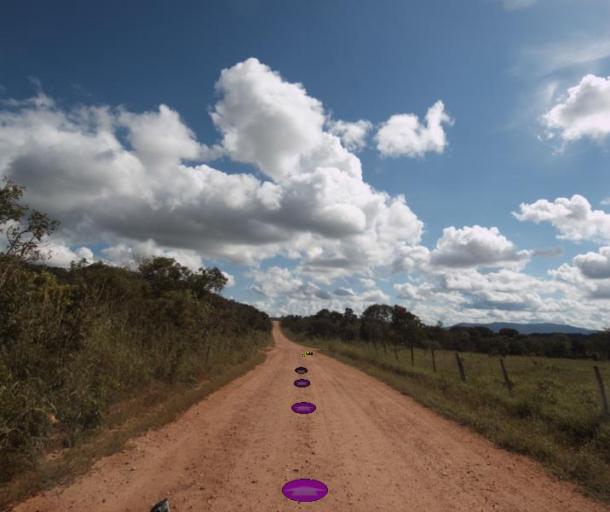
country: BR
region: Goias
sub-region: Jaragua
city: Jaragua
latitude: -15.8185
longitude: -49.1929
